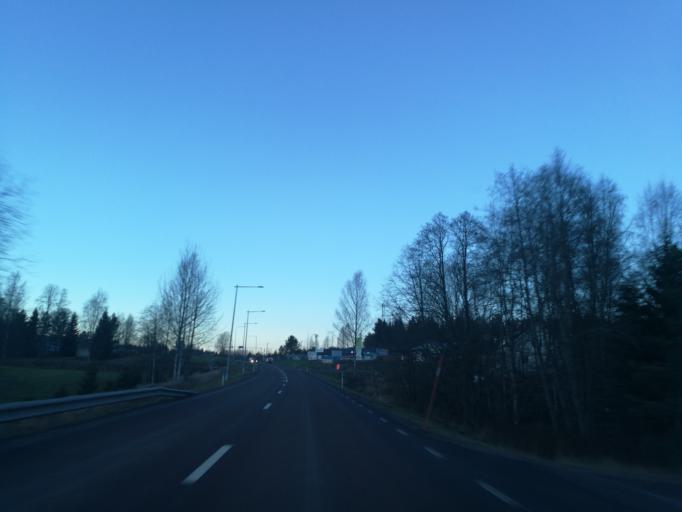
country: SE
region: Vaermland
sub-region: Eda Kommun
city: Charlottenberg
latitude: 59.9190
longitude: 12.2720
